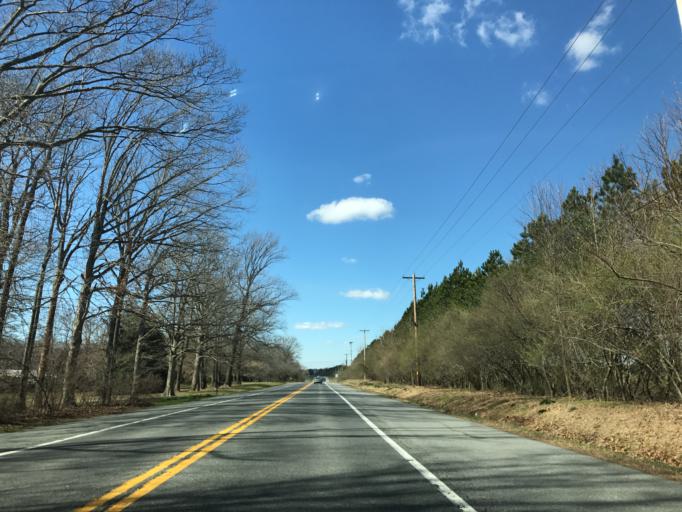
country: US
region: Maryland
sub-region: Queen Anne's County
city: Kingstown
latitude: 39.1797
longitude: -76.0025
